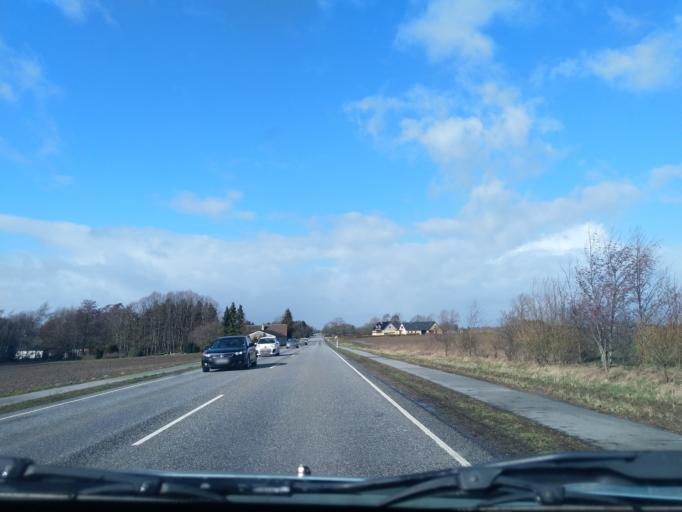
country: DK
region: Zealand
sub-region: Naestved Kommune
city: Naestved
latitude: 55.2806
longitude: 11.7186
